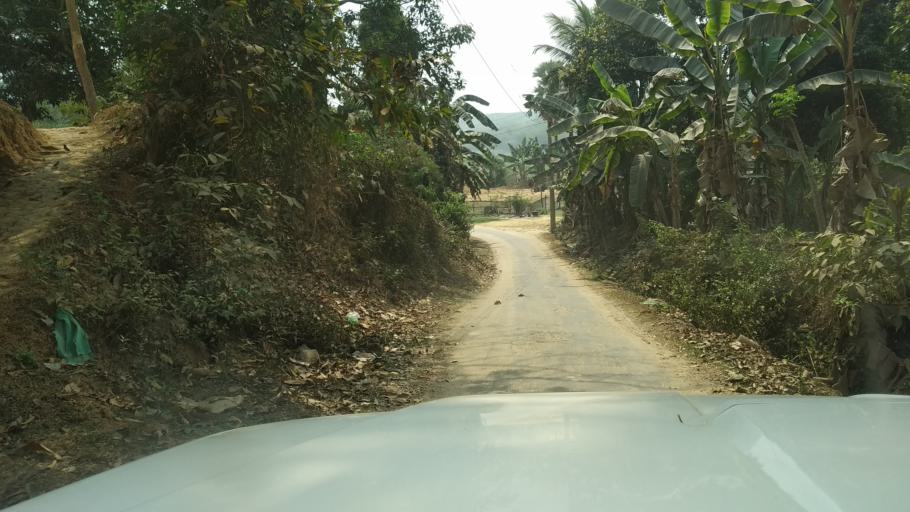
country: IN
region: Tripura
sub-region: West Tripura
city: Sonamura
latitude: 23.4315
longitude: 91.3119
